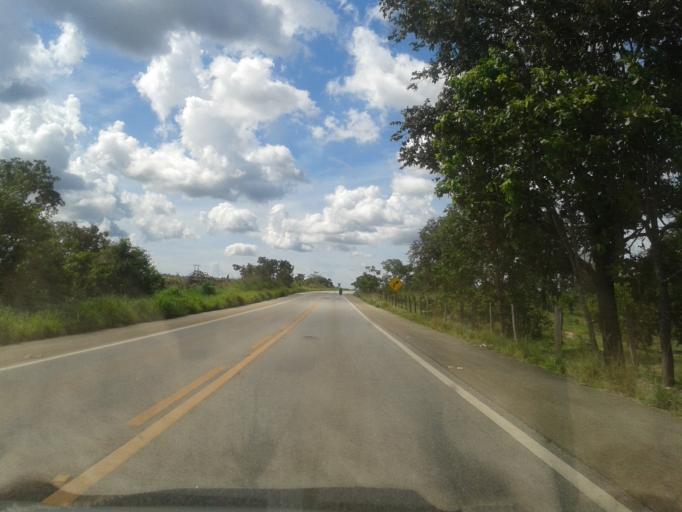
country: BR
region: Goias
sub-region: Itapuranga
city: Itapuranga
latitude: -15.5705
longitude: -50.2779
